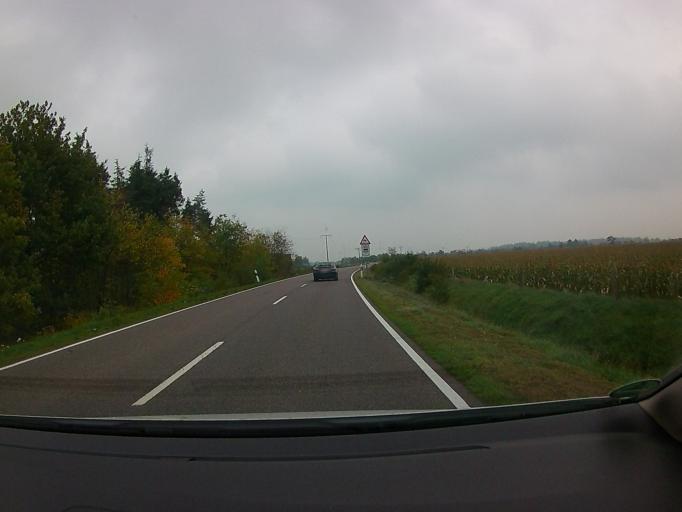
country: DE
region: Schleswig-Holstein
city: Goldebek
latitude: 54.6761
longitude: 9.1532
